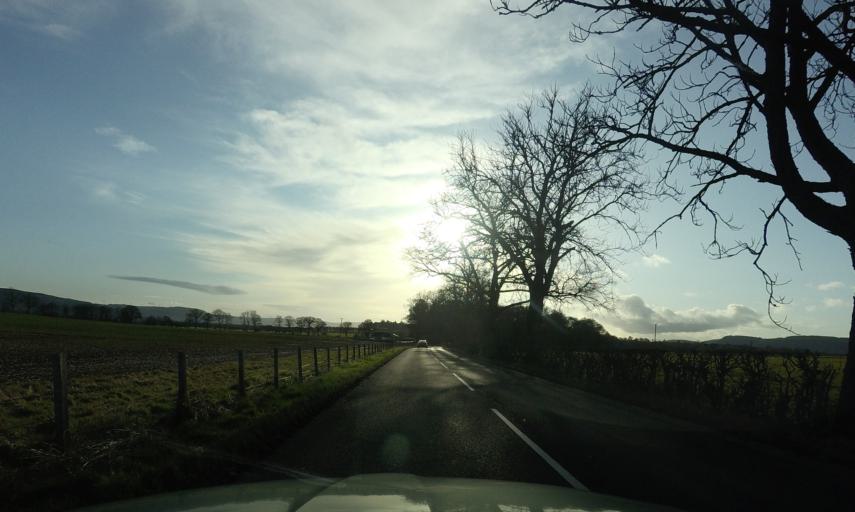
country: GB
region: Scotland
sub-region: Perth and Kinross
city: Errol
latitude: 56.3823
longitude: -3.2395
